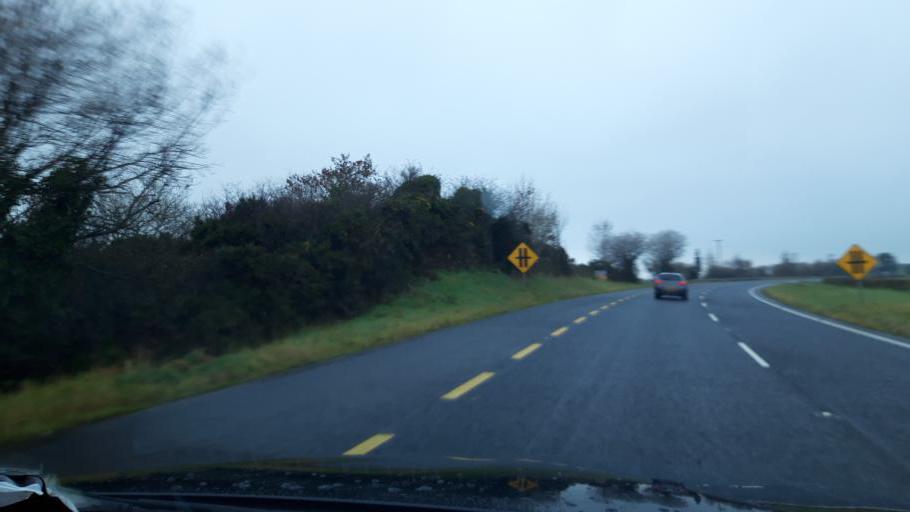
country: IE
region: Ulster
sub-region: County Donegal
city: Letterkenny
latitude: 54.9504
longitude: -7.6671
